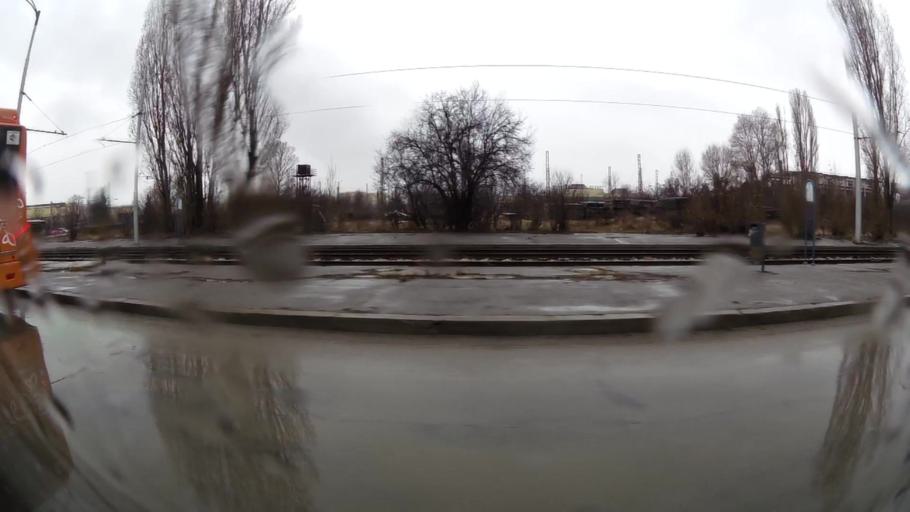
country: BG
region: Sofia-Capital
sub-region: Stolichna Obshtina
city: Sofia
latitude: 42.6562
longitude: 23.4146
